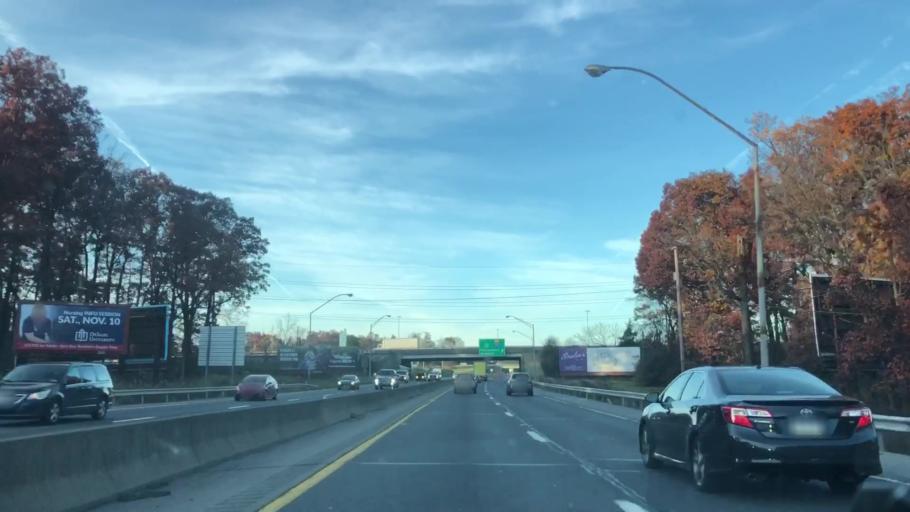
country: US
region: Pennsylvania
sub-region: Lehigh County
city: Wescosville
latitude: 40.5972
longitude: -75.5670
